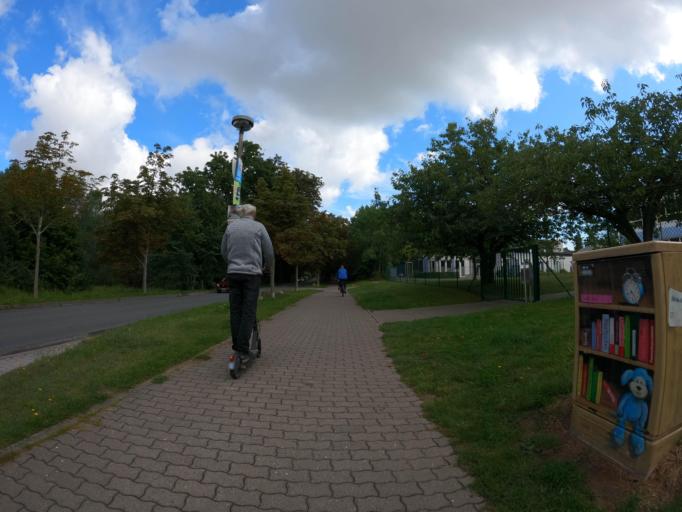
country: DE
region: Mecklenburg-Vorpommern
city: Putbus
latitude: 54.3490
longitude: 13.4849
